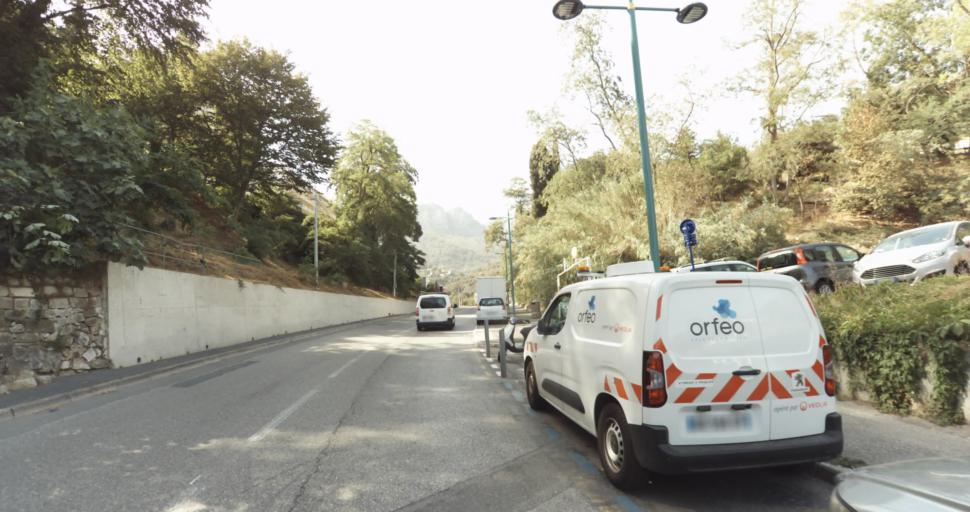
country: FR
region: Provence-Alpes-Cote d'Azur
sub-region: Departement des Alpes-Maritimes
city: Roquebrune-Cap-Martin
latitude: 43.7807
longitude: 7.4809
